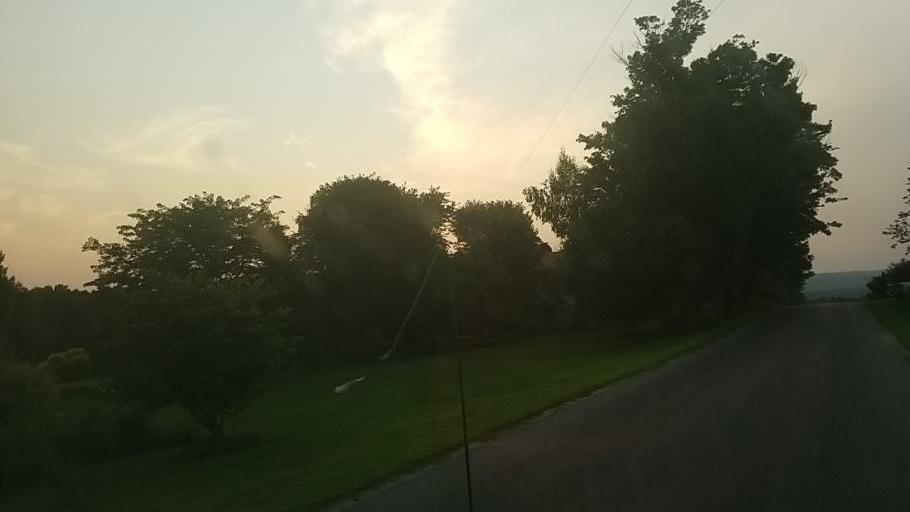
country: US
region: New York
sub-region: Montgomery County
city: Fonda
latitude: 42.9176
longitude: -74.4085
